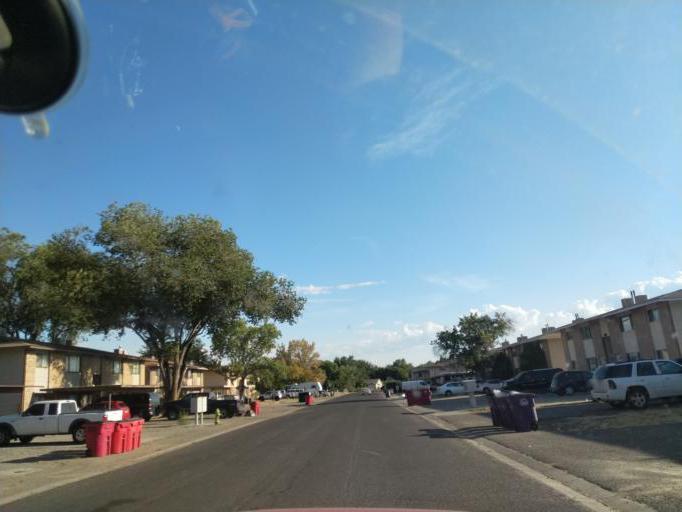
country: US
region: Colorado
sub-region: Mesa County
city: Clifton
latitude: 39.0753
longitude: -108.4566
